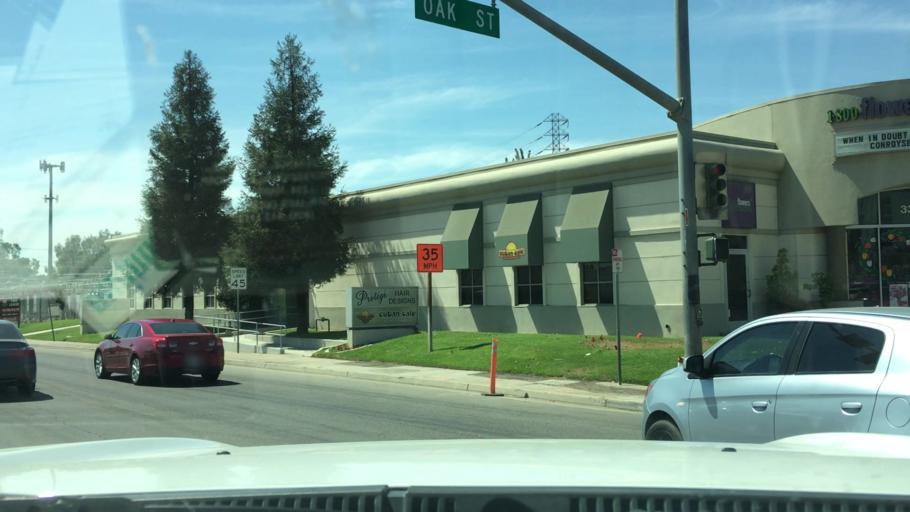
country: US
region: California
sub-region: Kern County
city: Bakersfield
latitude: 35.3735
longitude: -119.0388
